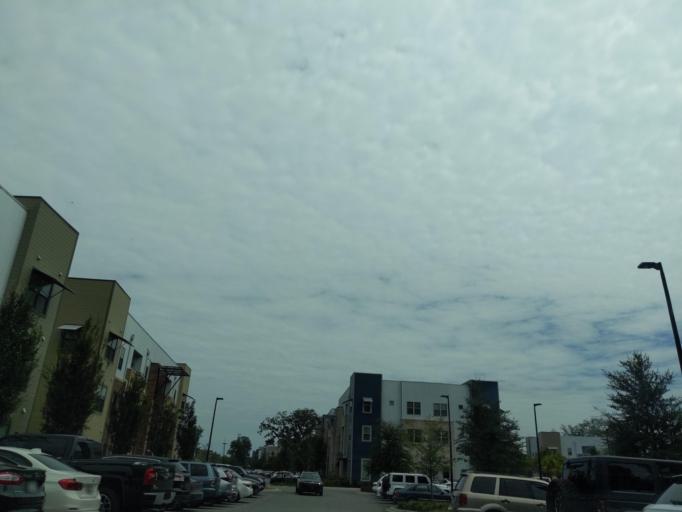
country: US
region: Florida
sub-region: Leon County
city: Tallahassee
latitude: 30.4345
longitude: -84.3000
